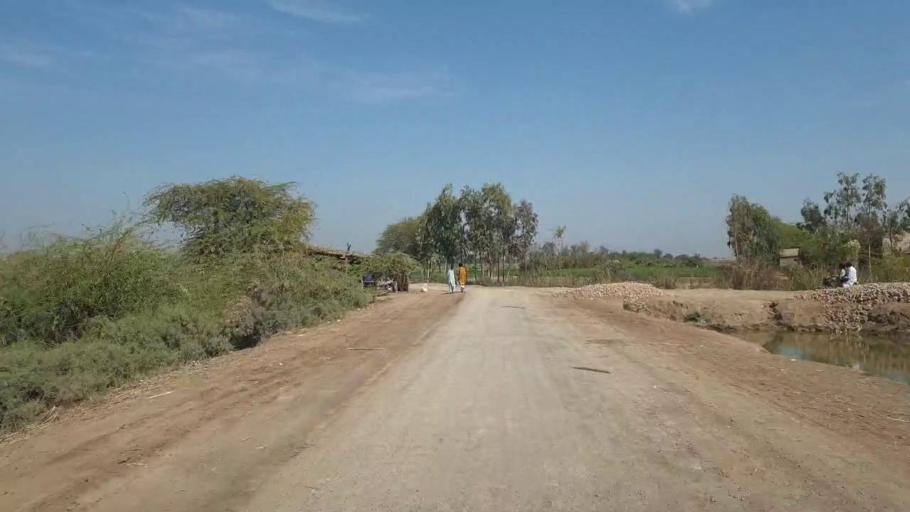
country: PK
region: Sindh
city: Samaro
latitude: 25.3820
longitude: 69.2597
